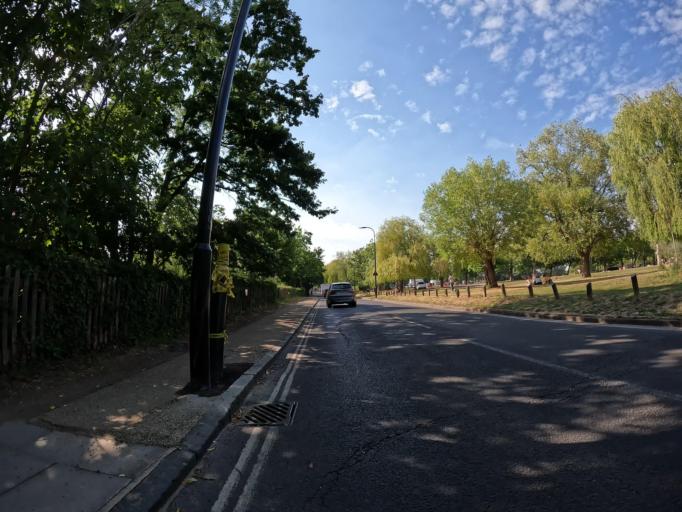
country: GB
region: England
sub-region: Greater London
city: Hadley Wood
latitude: 51.6668
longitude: -0.1639
